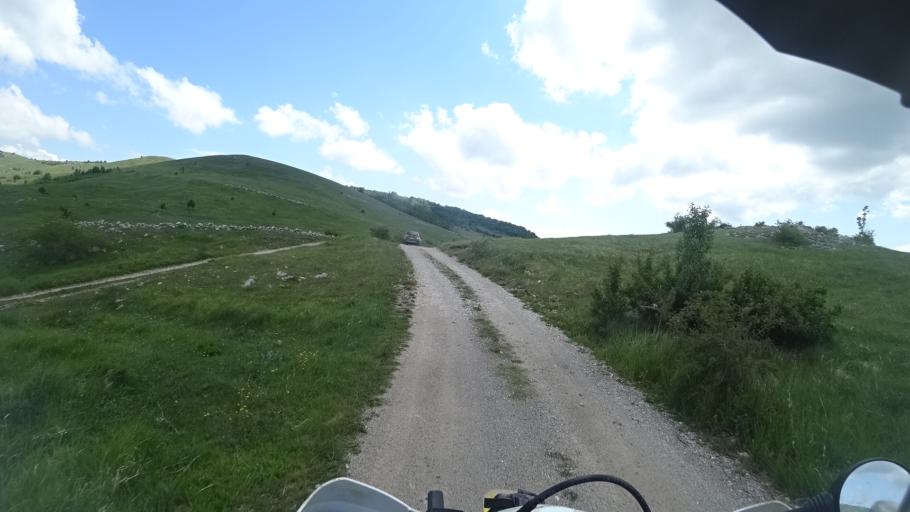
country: HR
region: Zadarska
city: Gracac
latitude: 44.2990
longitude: 15.9459
